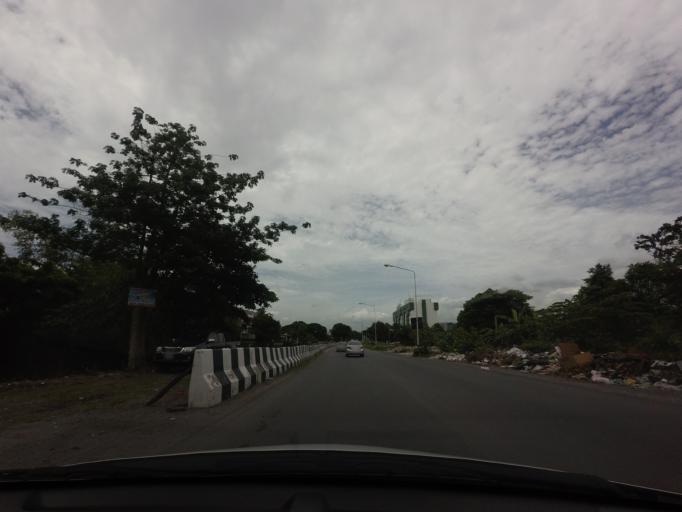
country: TH
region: Bangkok
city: Lak Si
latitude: 13.8572
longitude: 100.5778
